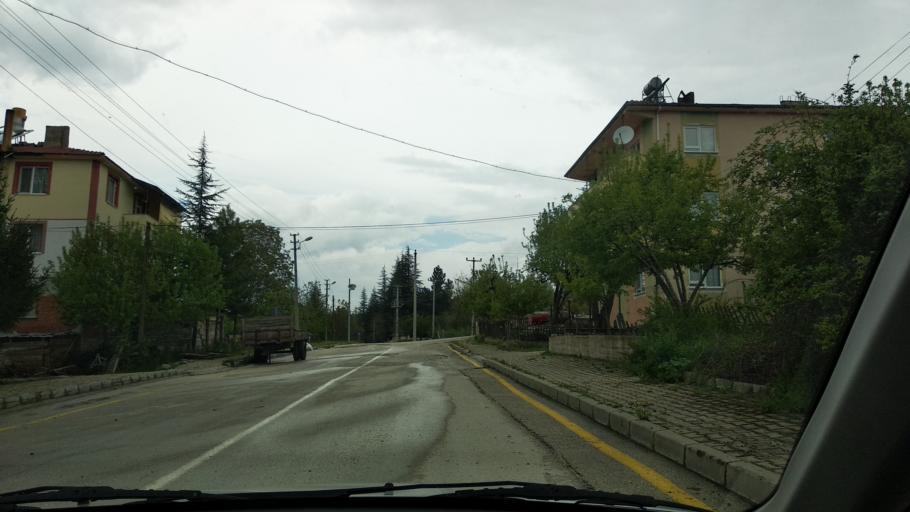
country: TR
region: Bolu
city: Seben
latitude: 40.4139
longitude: 31.5664
